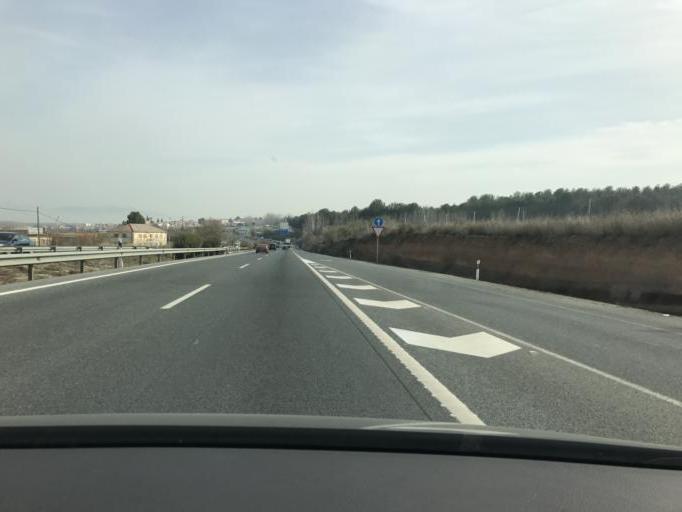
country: ES
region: Andalusia
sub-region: Provincia de Granada
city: Lachar
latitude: 37.1942
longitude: -3.8523
